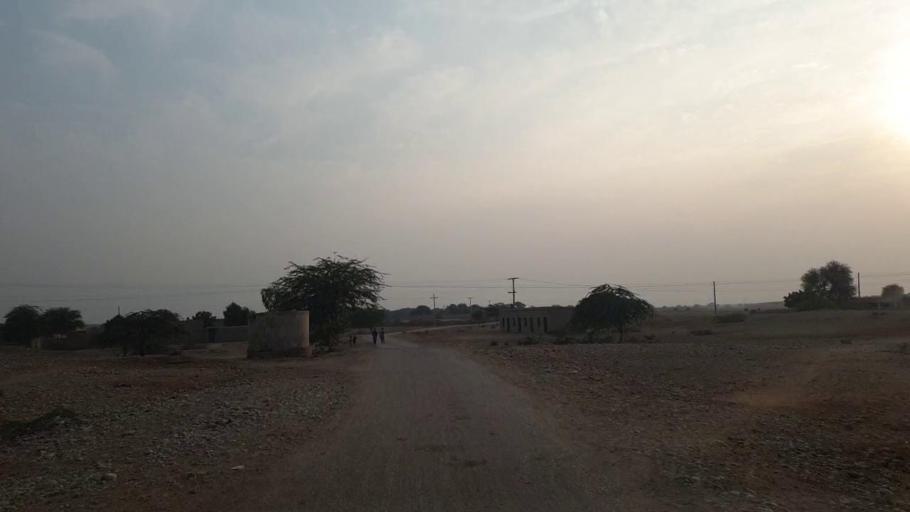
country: PK
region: Sindh
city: Sann
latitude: 26.1640
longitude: 68.0077
